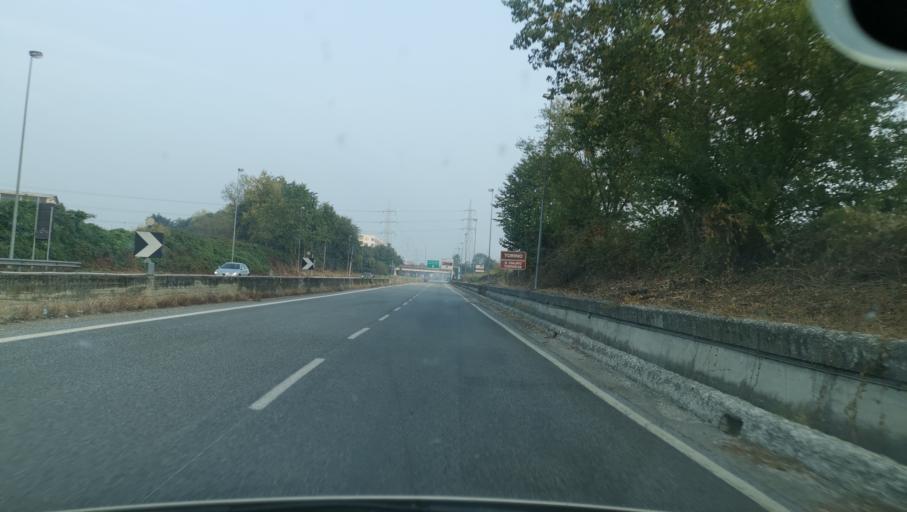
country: IT
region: Piedmont
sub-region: Provincia di Torino
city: San Mauro Torinese
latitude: 45.1133
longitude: 7.7365
